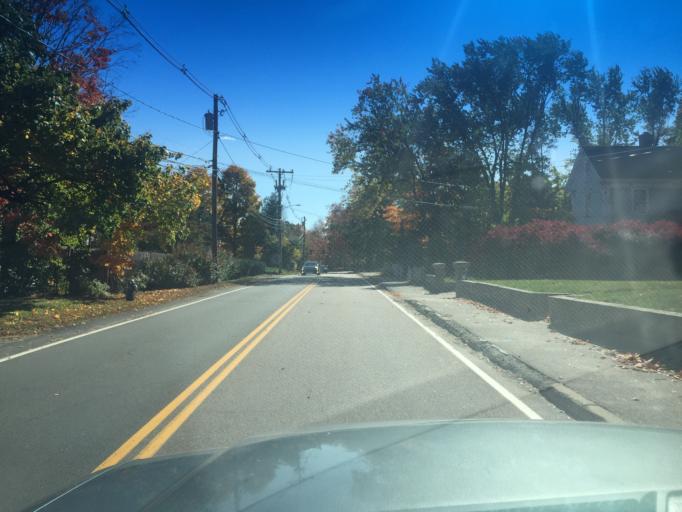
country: US
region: Massachusetts
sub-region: Norfolk County
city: Medway
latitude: 42.1496
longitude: -71.4253
